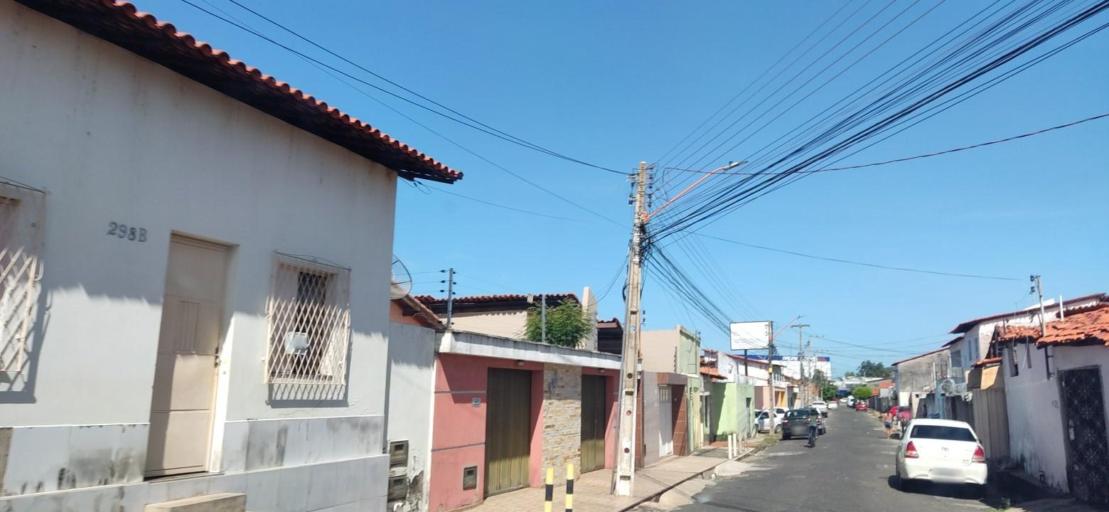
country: BR
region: Piaui
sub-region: Teresina
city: Teresina
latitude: -5.0981
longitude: -42.8000
